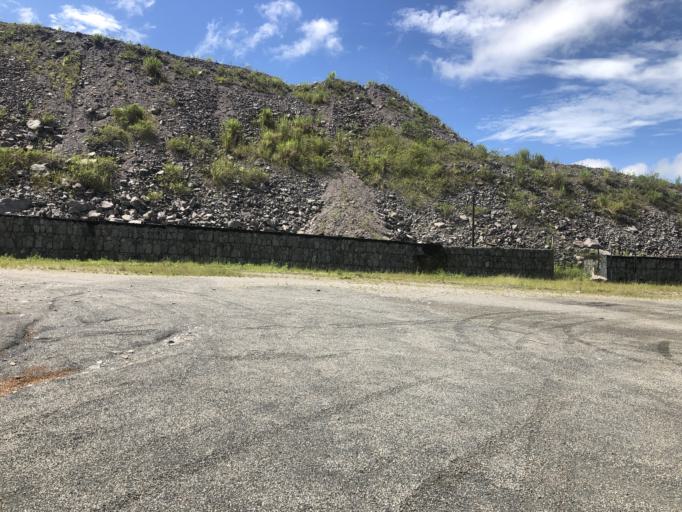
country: SL
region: Eastern Province
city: Koidu
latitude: 8.6353
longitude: -10.9699
